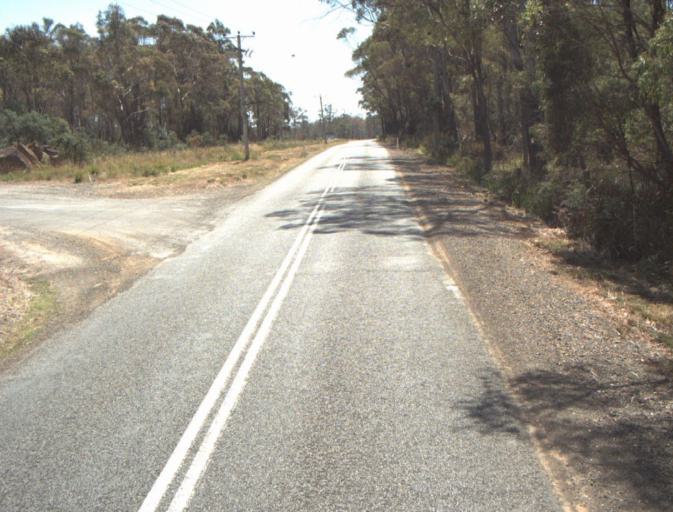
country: AU
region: Tasmania
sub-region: Launceston
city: Mayfield
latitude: -41.3262
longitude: 147.1385
